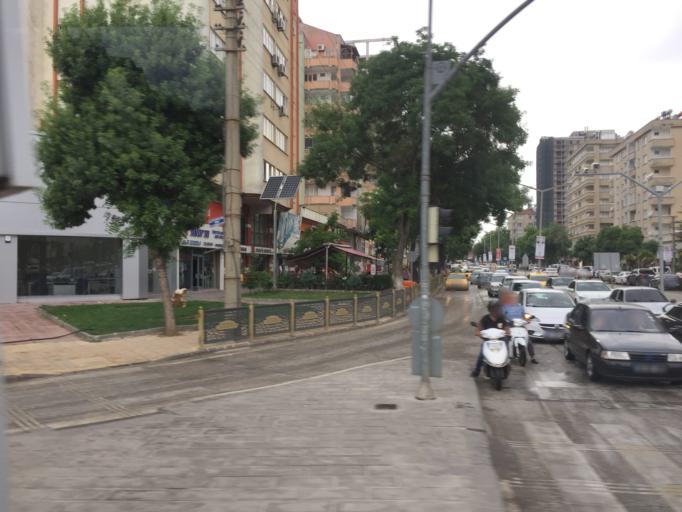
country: TR
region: Gaziantep
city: Gaziantep
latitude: 37.0723
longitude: 37.3721
